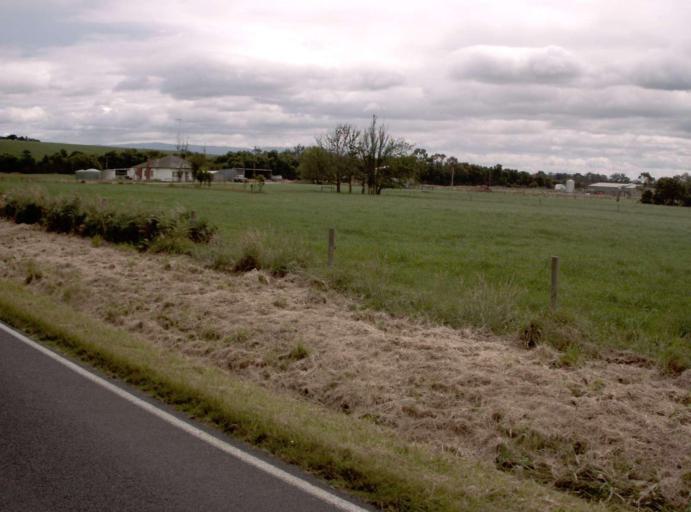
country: AU
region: Victoria
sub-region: Latrobe
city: Moe
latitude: -38.1749
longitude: 146.1454
